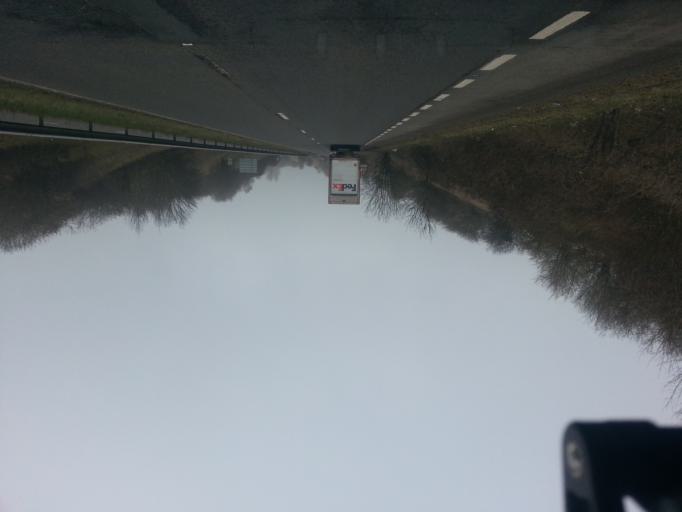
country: GB
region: England
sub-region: Oxfordshire
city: Boars Hill
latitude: 51.7349
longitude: -1.3281
